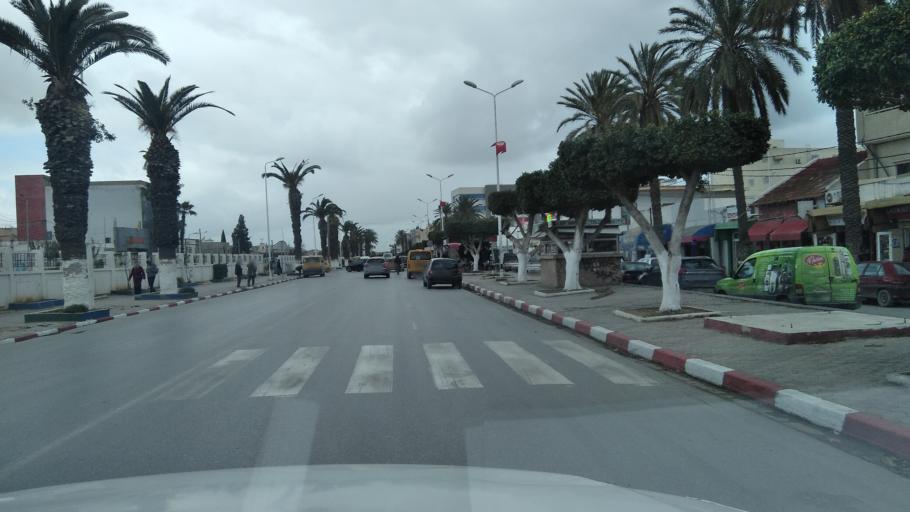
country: TN
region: Bin 'Arus
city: Ben Arous
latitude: 36.7542
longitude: 10.2221
